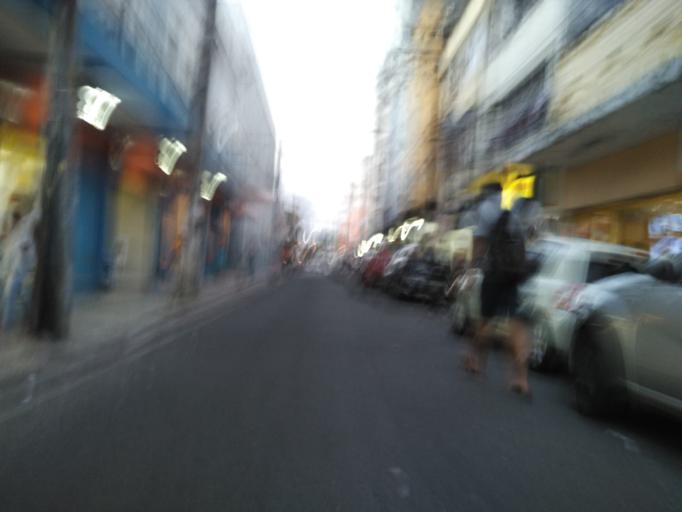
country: BR
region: Pernambuco
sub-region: Recife
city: Recife
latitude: -8.0657
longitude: -34.8814
